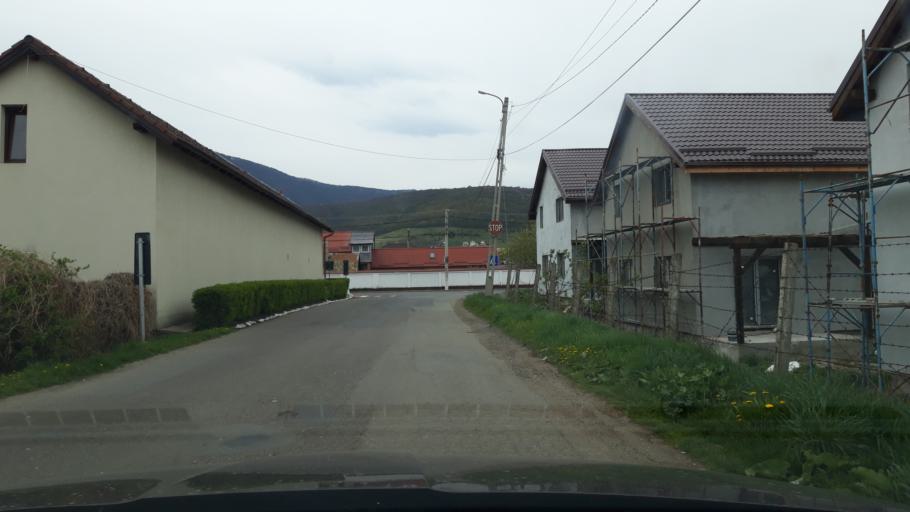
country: RO
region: Brasov
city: Codlea
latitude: 45.7013
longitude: 25.4564
